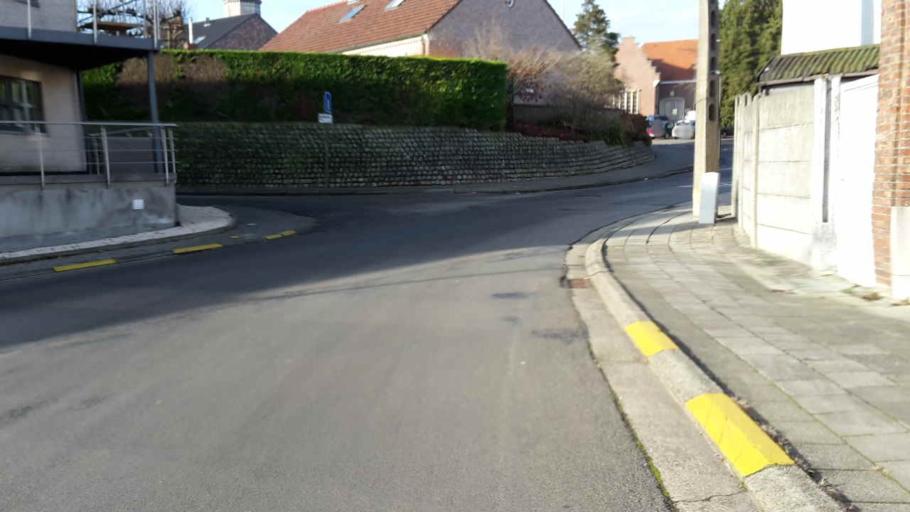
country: BE
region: Flanders
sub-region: Provincie Vlaams-Brabant
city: Hoegaarden
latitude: 50.8185
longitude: 4.8888
